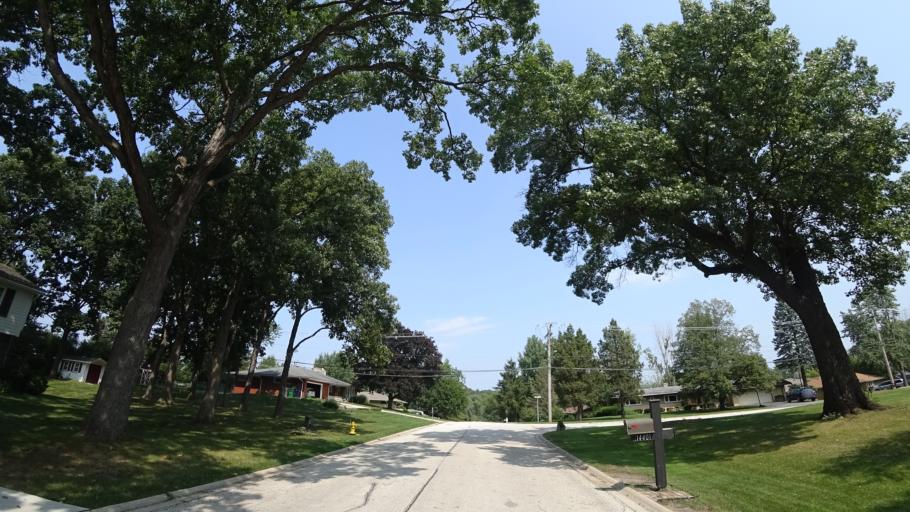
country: US
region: Illinois
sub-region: Cook County
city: Orland Park
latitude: 41.6279
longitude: -87.8724
